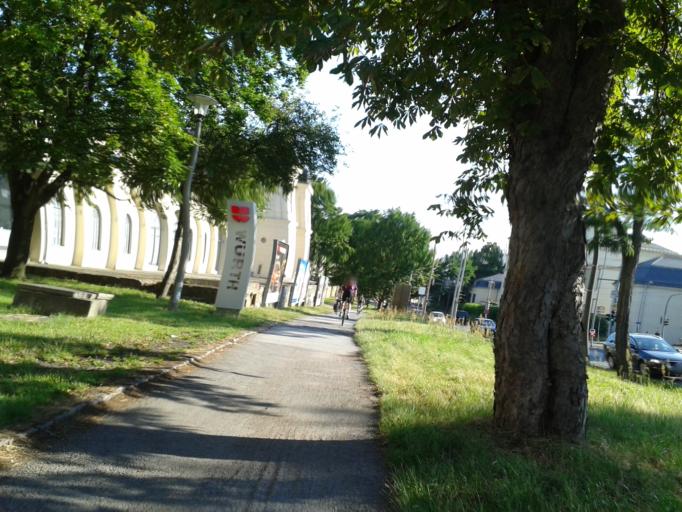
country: DE
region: Saxony
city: Albertstadt
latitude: 51.0806
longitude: 13.7596
